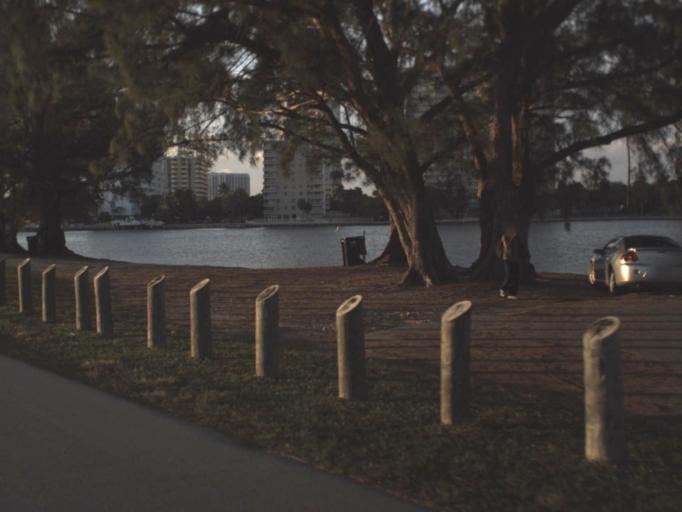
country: US
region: Florida
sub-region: Miami-Dade County
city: Miami
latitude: 25.7465
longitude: -80.1987
